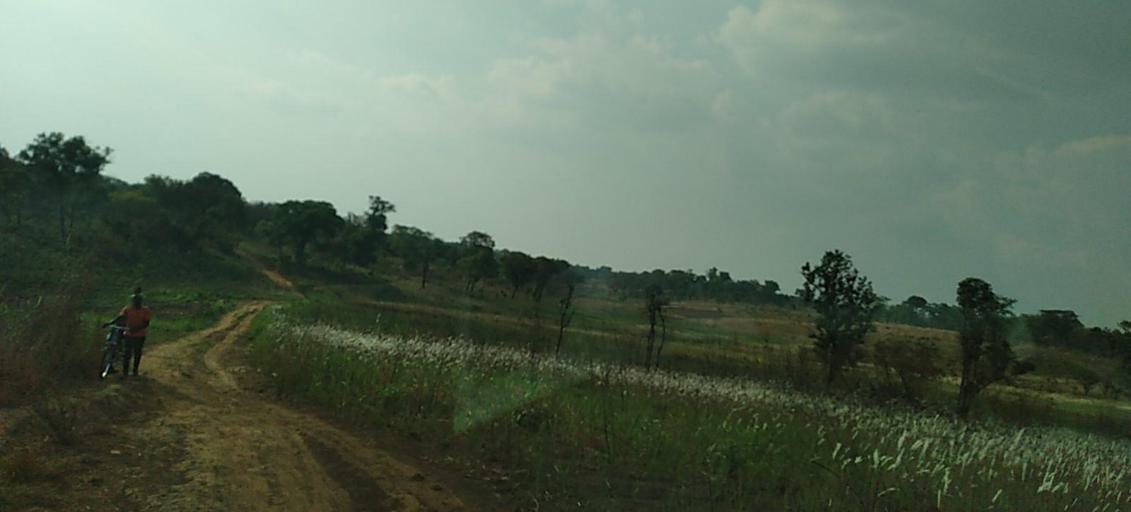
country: ZM
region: North-Western
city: Solwezi
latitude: -12.0665
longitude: 26.1782
